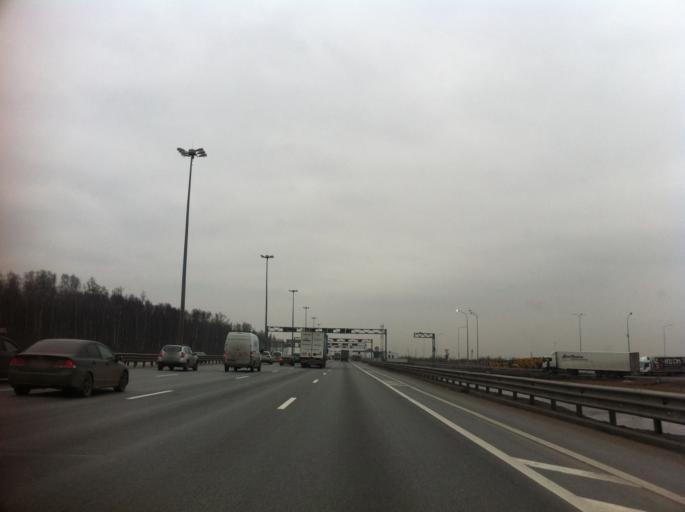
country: RU
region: Leningrad
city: Rybatskoye
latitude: 59.8799
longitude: 30.5282
